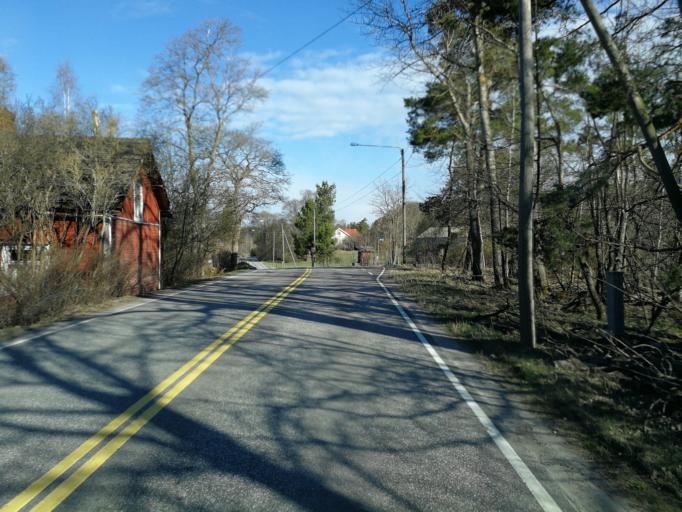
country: FI
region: Uusimaa
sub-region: Helsinki
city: Kirkkonummi
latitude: 60.2200
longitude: 24.4721
